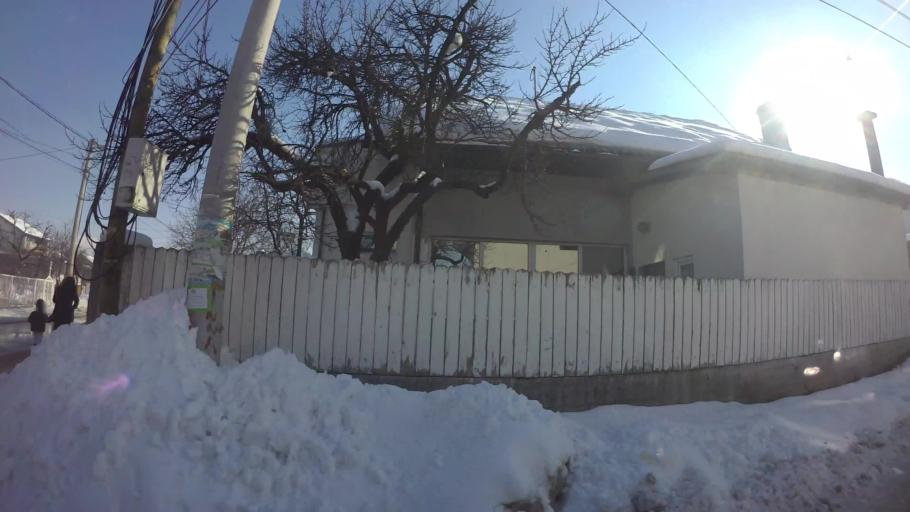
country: BA
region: Federation of Bosnia and Herzegovina
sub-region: Kanton Sarajevo
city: Sarajevo
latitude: 43.8155
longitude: 18.3127
